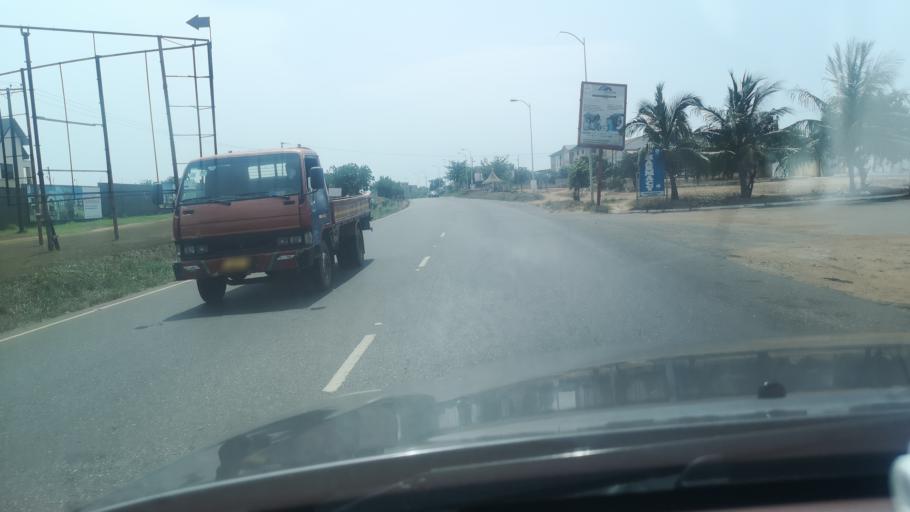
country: GH
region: Greater Accra
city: Nungua
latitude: 5.6158
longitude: -0.0620
